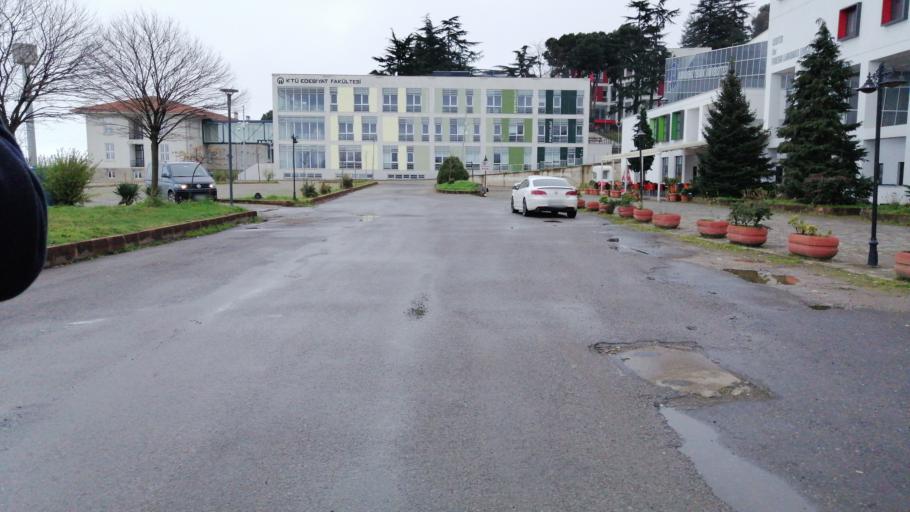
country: TR
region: Trabzon
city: Trabzon
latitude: 40.9991
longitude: 39.7678
